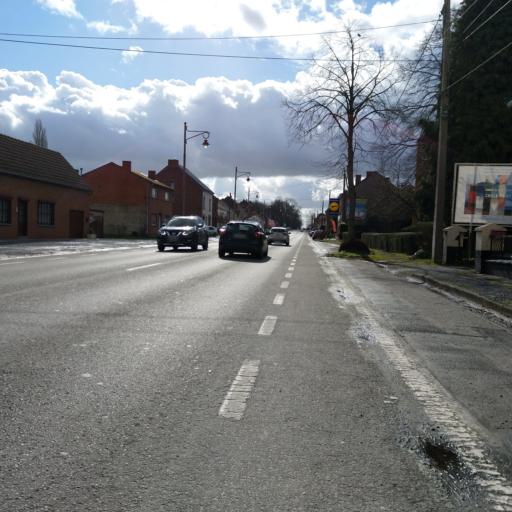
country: BE
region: Wallonia
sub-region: Province du Hainaut
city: Mons
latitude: 50.4898
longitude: 3.9420
